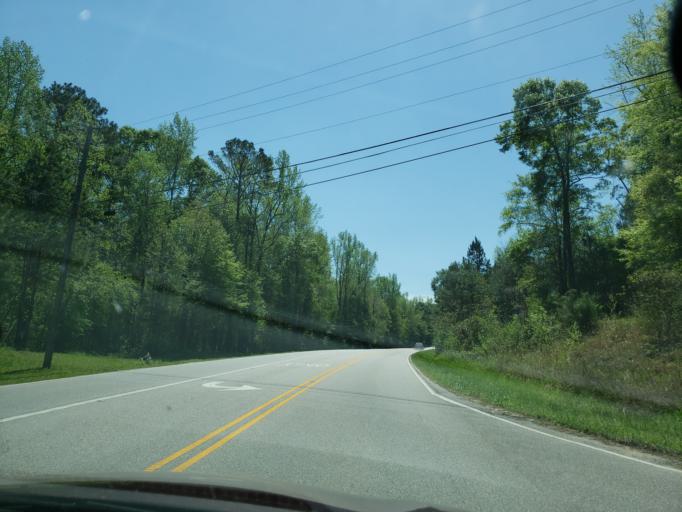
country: US
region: Alabama
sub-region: Lee County
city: Auburn
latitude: 32.6404
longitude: -85.5031
